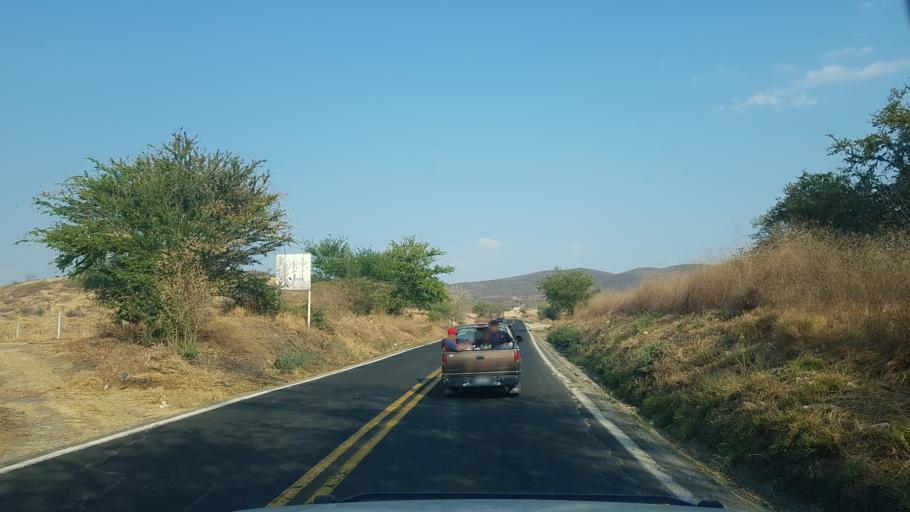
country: MX
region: Puebla
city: Calmeca
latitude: 18.6430
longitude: -98.6222
